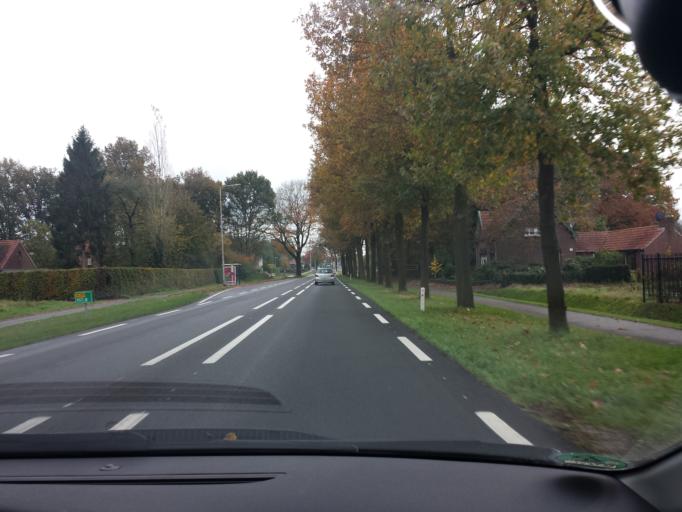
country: NL
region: Gelderland
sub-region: Gemeente Groesbeek
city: Bredeweg
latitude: 51.7273
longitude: 5.9427
